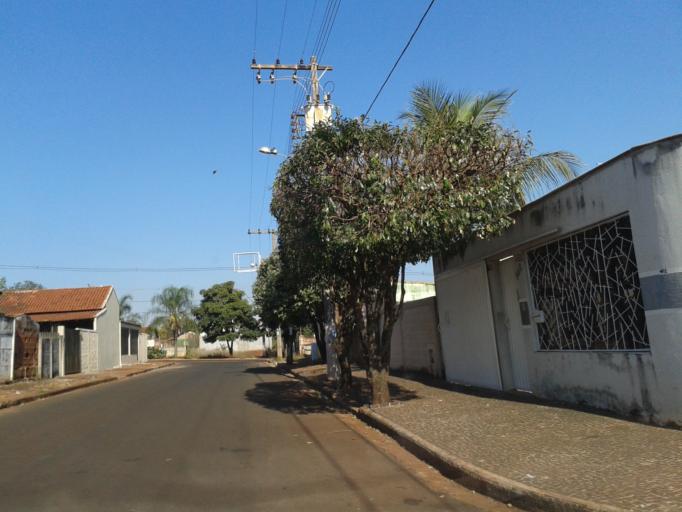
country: BR
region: Minas Gerais
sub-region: Ituiutaba
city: Ituiutaba
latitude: -18.9701
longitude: -49.4869
